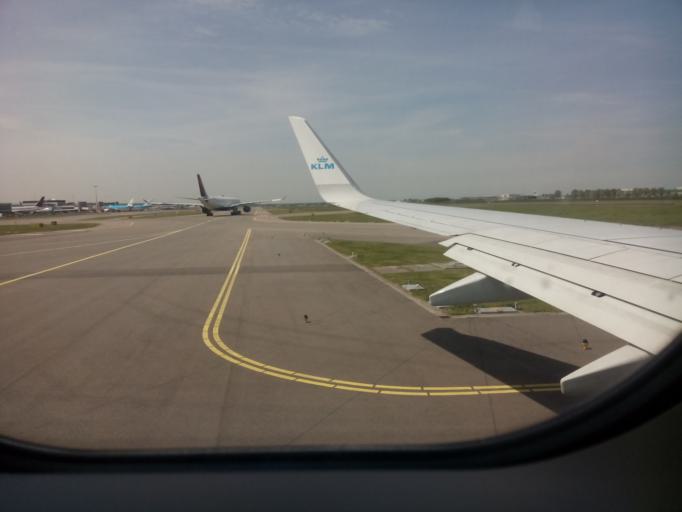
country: NL
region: North Holland
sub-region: Gemeente Aalsmeer
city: Aalsmeer
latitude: 52.3159
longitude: 4.7751
